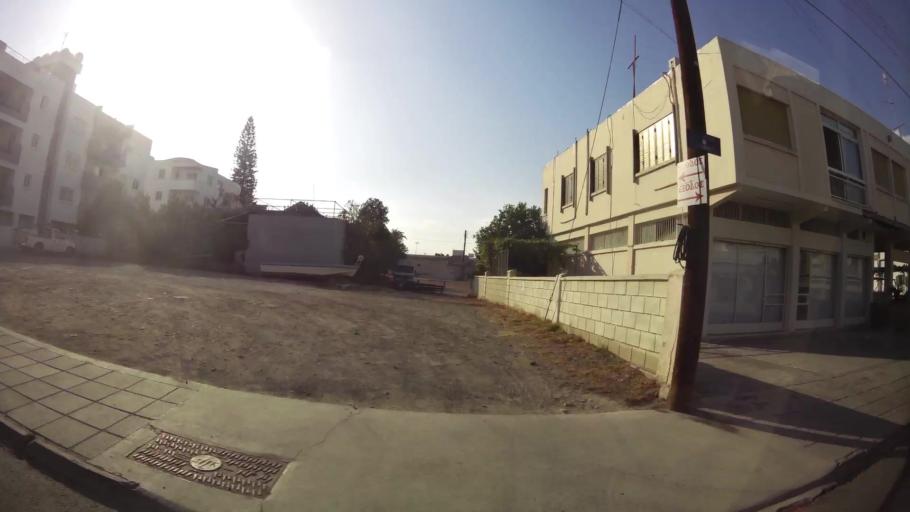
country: CY
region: Lefkosia
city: Nicosia
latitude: 35.1752
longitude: 33.3335
